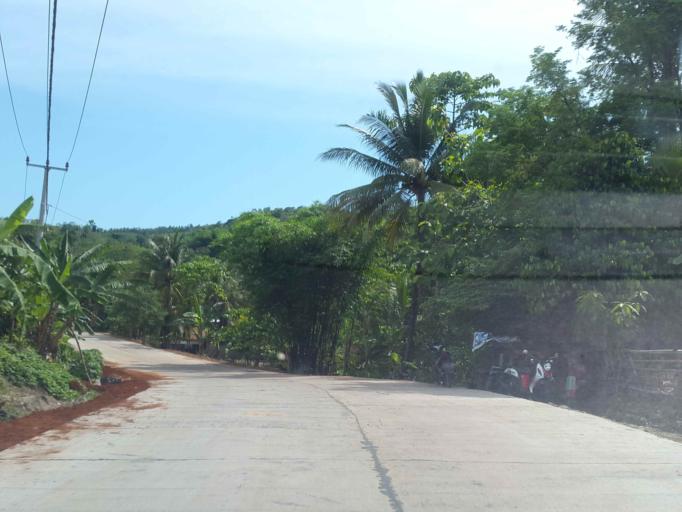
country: ID
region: Banten
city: Citeureup
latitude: -6.5022
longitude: 105.6426
